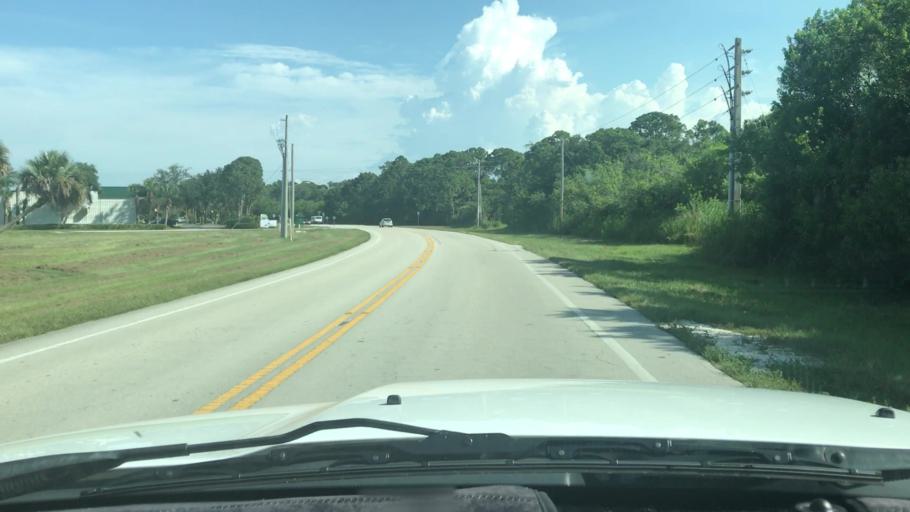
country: US
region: Florida
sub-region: Indian River County
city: Gifford
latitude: 27.6568
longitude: -80.4322
